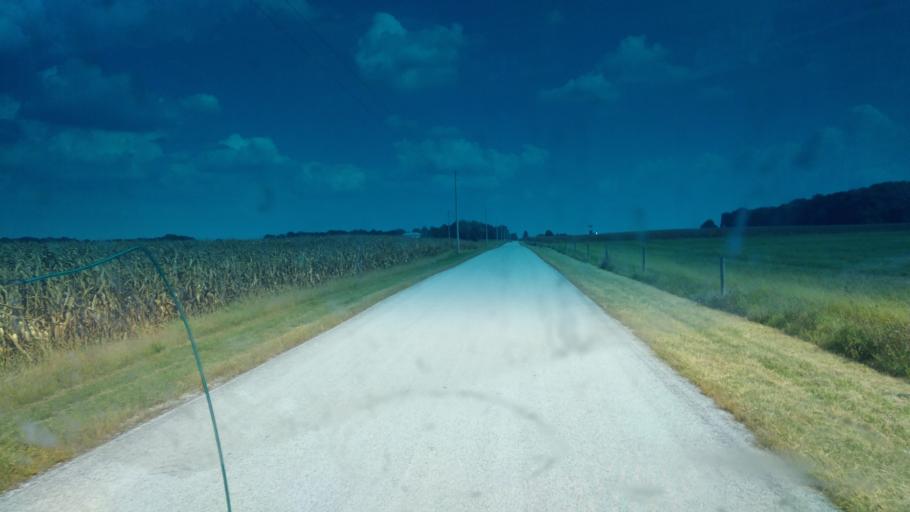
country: US
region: Ohio
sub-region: Hardin County
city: Kenton
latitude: 40.6600
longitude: -83.7082
